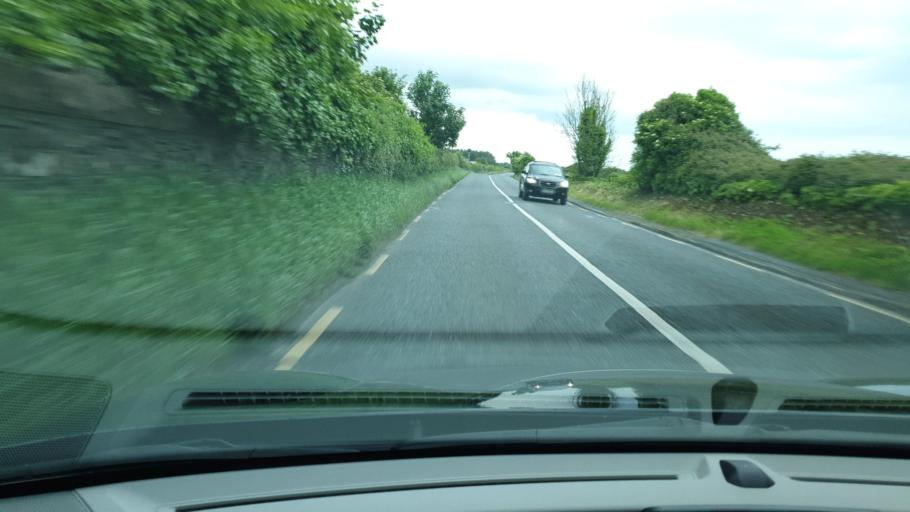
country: IE
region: Leinster
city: Balrothery
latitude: 53.5931
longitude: -6.1580
